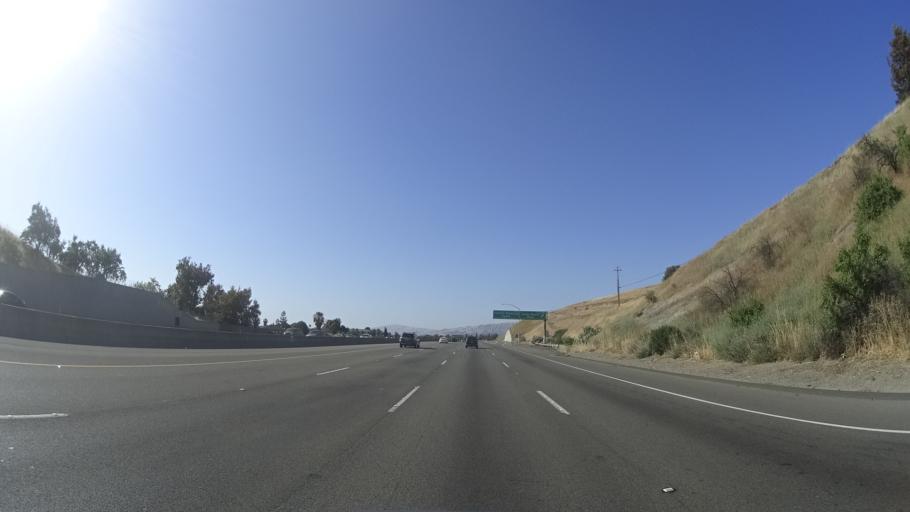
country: US
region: California
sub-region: Santa Clara County
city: Seven Trees
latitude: 37.2912
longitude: -121.8097
